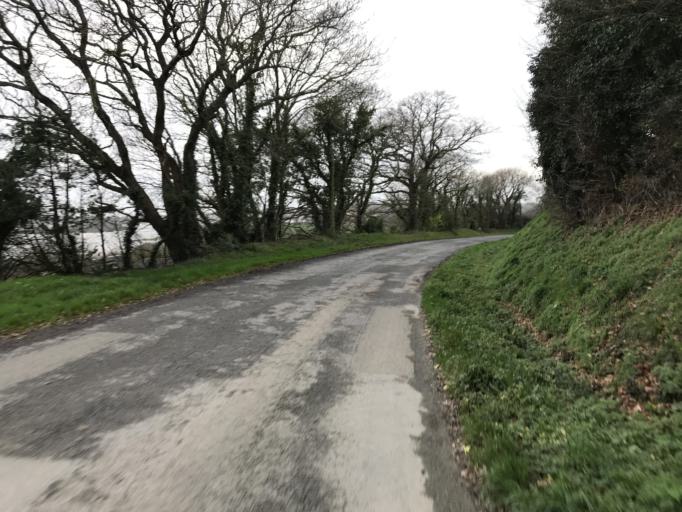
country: FR
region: Brittany
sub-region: Departement du Finistere
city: Daoulas
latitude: 48.3564
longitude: -4.2792
